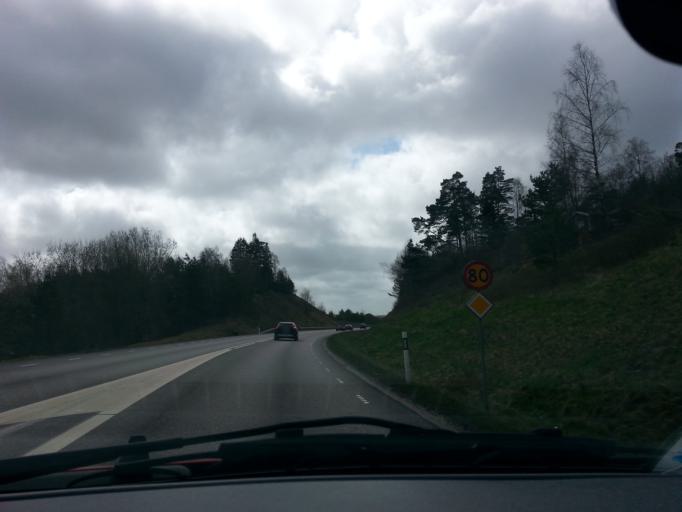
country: SE
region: Vaestra Goetaland
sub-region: Lerums Kommun
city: Grabo
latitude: 57.8505
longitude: 12.3084
